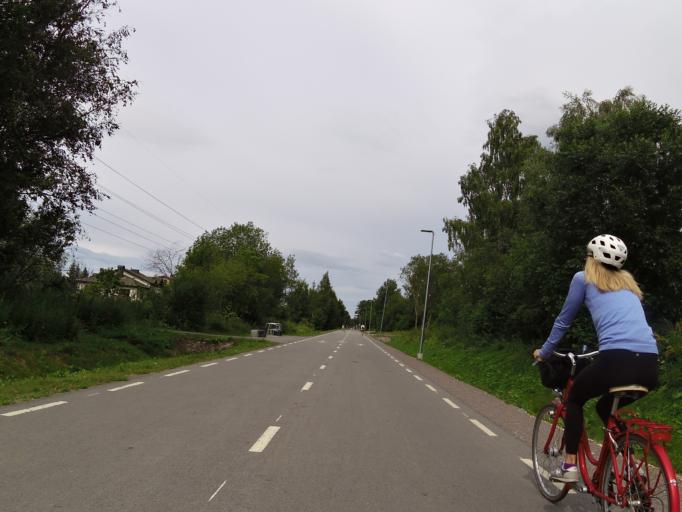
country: EE
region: Harju
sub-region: Tallinna linn
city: Tallinn
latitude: 59.4222
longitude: 24.6771
